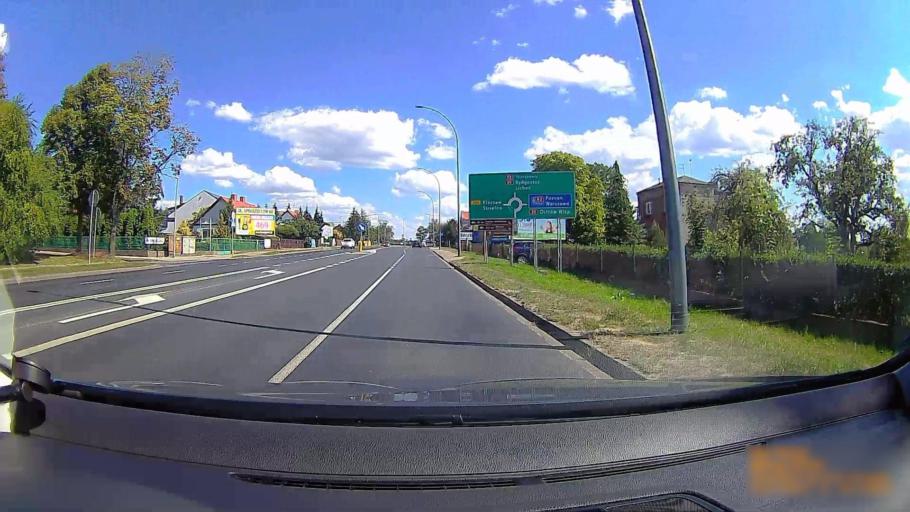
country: PL
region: Greater Poland Voivodeship
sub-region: Konin
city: Konin
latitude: 52.2269
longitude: 18.2404
